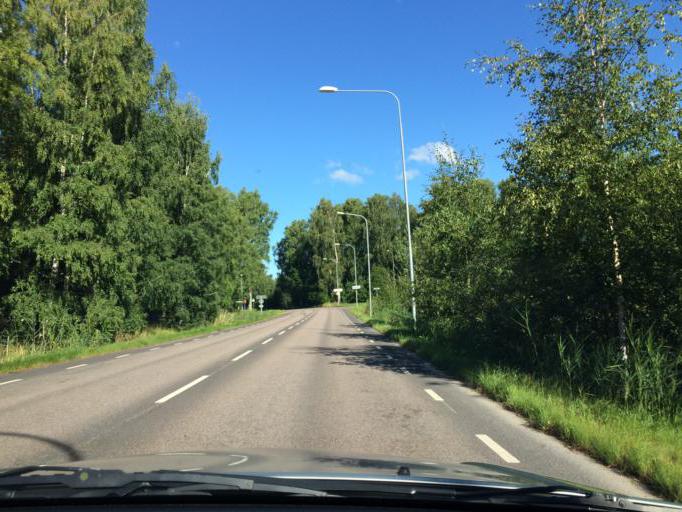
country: SE
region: Vaestmanland
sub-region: Vasteras
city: Vasteras
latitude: 59.5915
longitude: 16.6068
